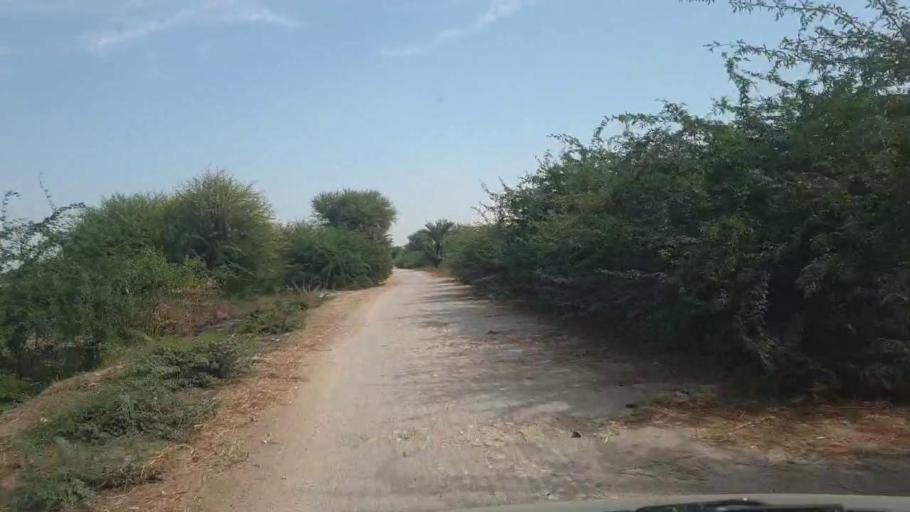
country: PK
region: Sindh
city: Tando Bago
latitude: 24.9116
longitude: 69.0366
